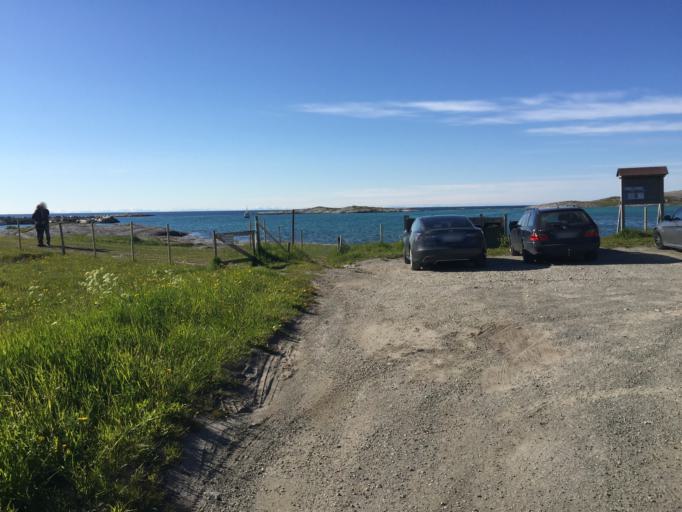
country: NO
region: Nordland
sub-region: Bodo
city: Loding
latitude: 67.4114
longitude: 14.6280
